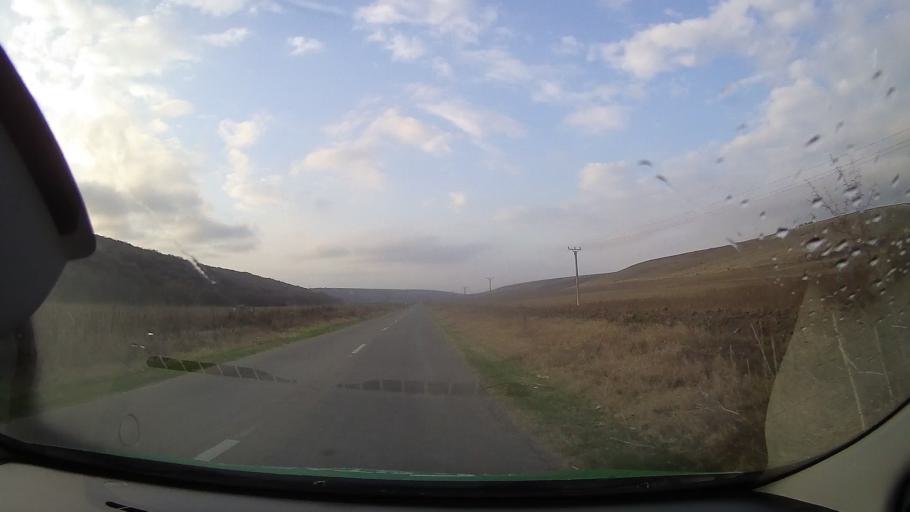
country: RO
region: Constanta
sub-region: Comuna Dobromir
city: Dobromir
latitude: 44.0274
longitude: 27.8642
